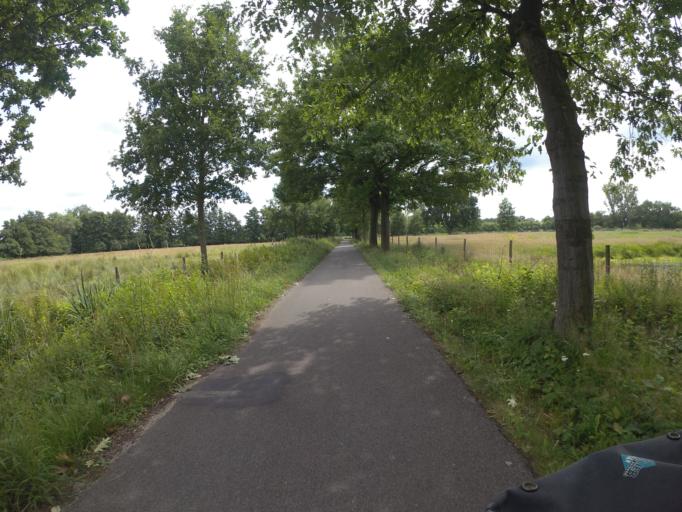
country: NL
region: North Brabant
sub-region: Gemeente Eindhoven
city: Muschberg en Geestenberg
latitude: 51.4362
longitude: 5.5361
